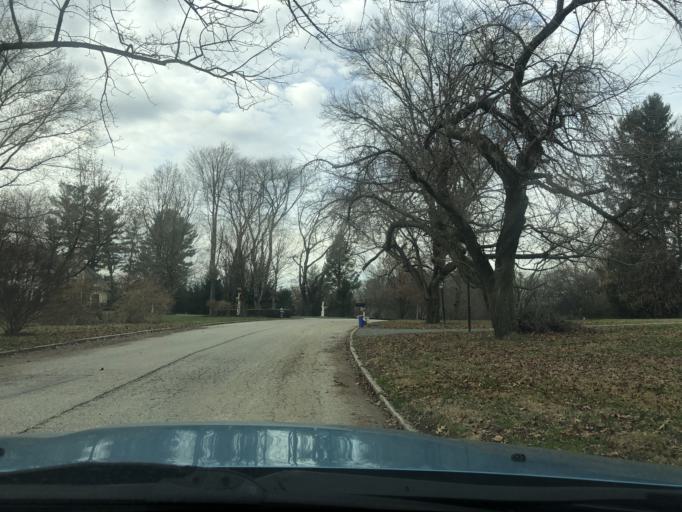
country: US
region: Pennsylvania
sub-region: Delaware County
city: Radnor
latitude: 40.0221
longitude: -75.3563
